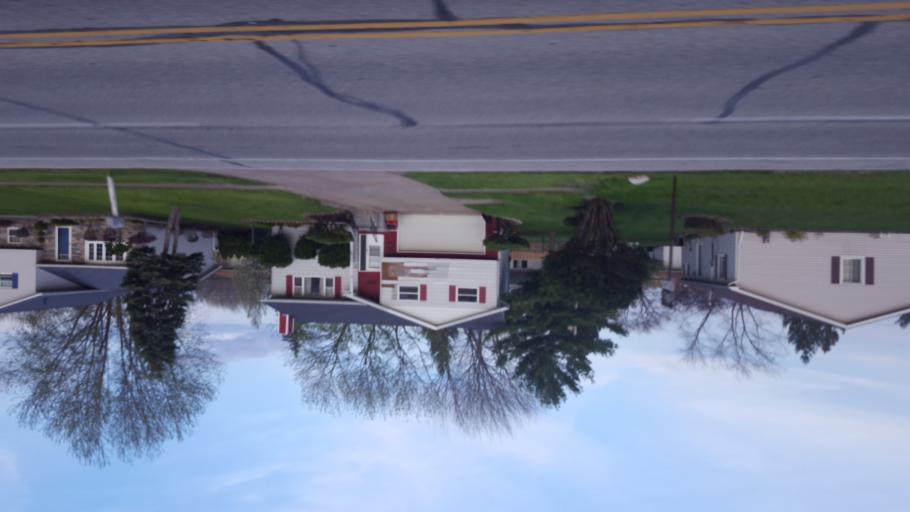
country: US
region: Ohio
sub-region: Lorain County
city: Lorain
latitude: 41.4357
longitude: -82.2025
